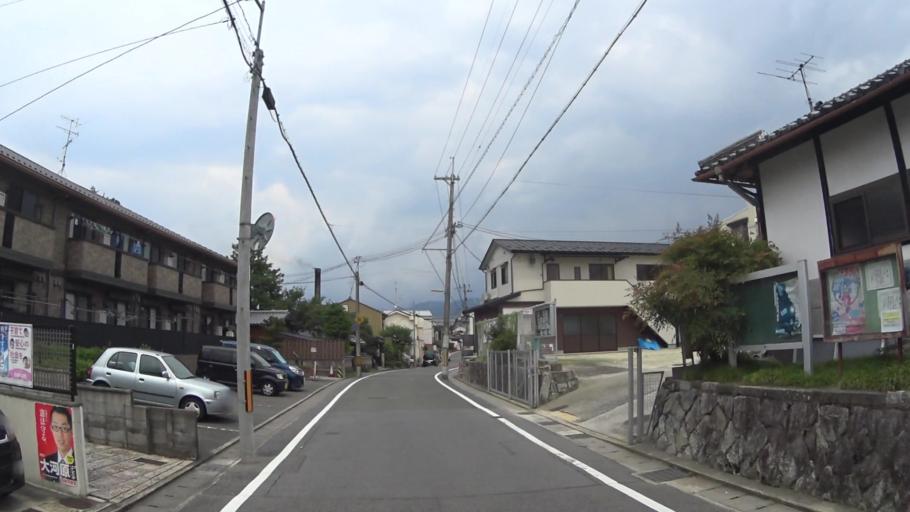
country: JP
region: Kyoto
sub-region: Kyoto-shi
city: Kamigyo-ku
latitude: 35.0448
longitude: 135.7940
